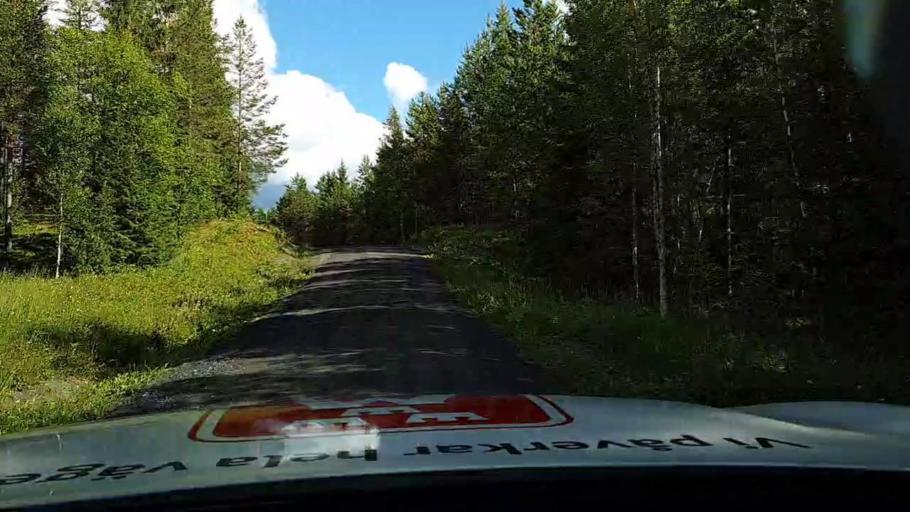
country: SE
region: Jaemtland
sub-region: Krokoms Kommun
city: Valla
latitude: 63.3242
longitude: 13.7474
